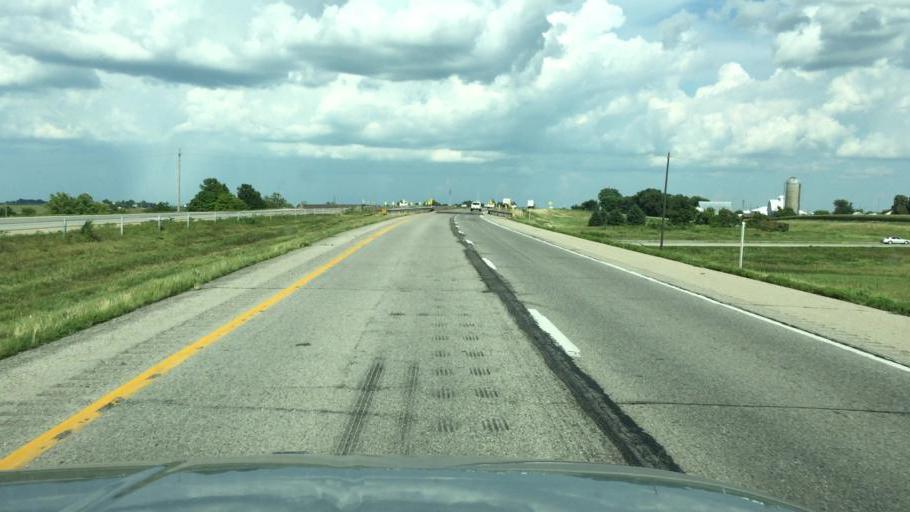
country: US
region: Iowa
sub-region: Poweshiek County
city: Grinnell
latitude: 41.6961
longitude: -92.7293
